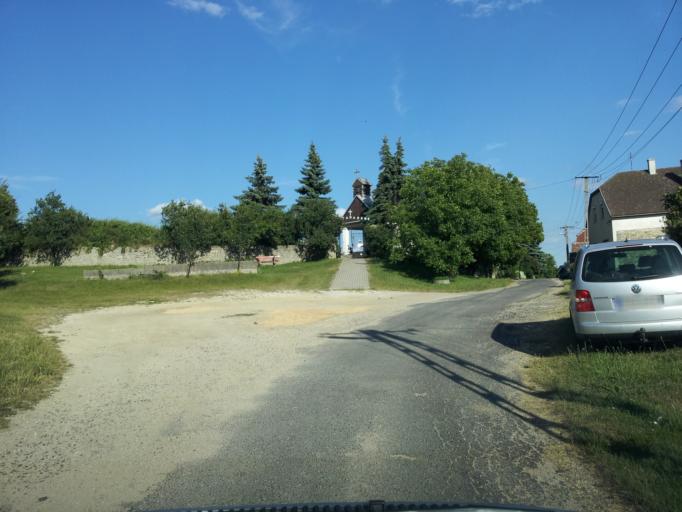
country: HU
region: Veszprem
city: Zirc
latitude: 47.2050
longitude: 17.8736
